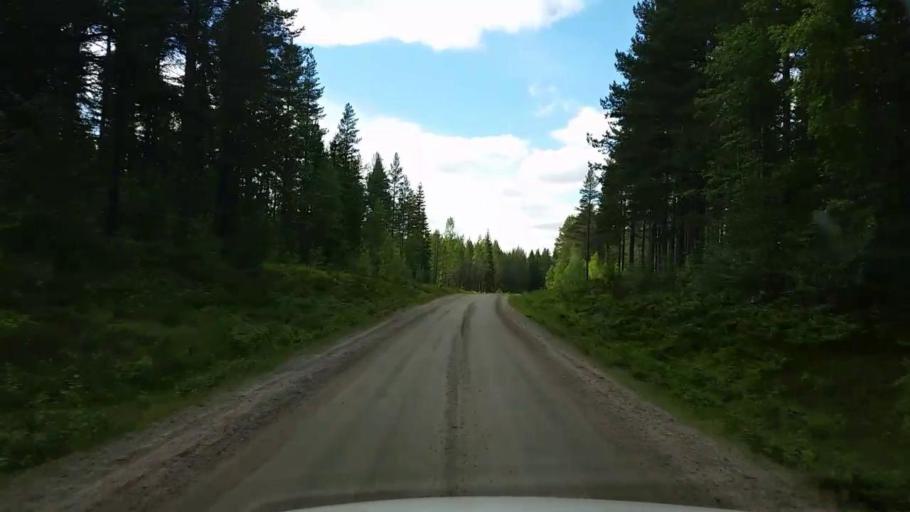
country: SE
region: Gaevleborg
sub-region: Ovanakers Kommun
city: Alfta
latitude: 61.5587
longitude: 15.9818
